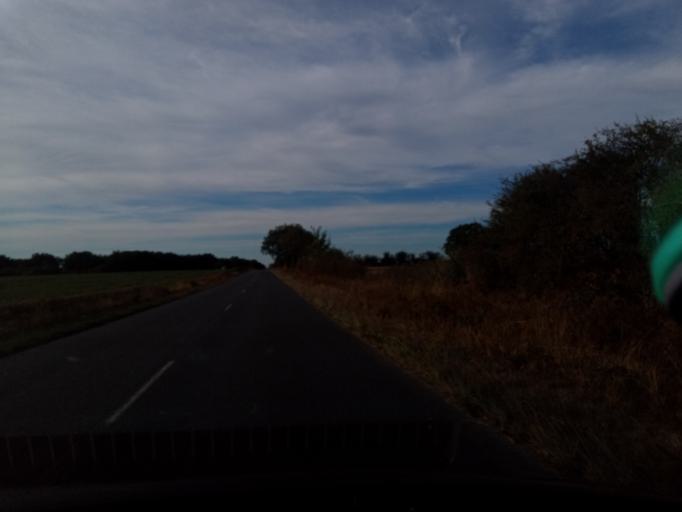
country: FR
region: Poitou-Charentes
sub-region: Departement de la Vienne
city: Montmorillon
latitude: 46.4092
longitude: 0.8879
